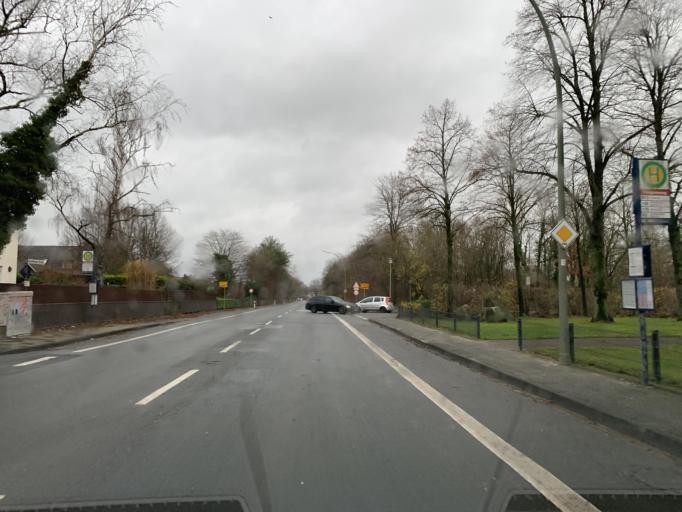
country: DE
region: North Rhine-Westphalia
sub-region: Regierungsbezirk Munster
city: Steinfurt
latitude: 52.1324
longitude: 7.3984
